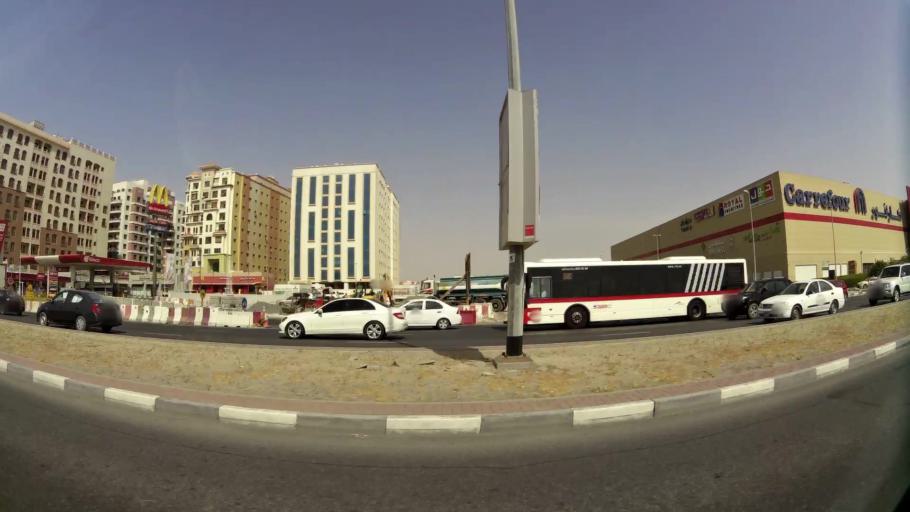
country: AE
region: Ash Shariqah
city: Sharjah
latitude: 25.2839
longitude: 55.3978
